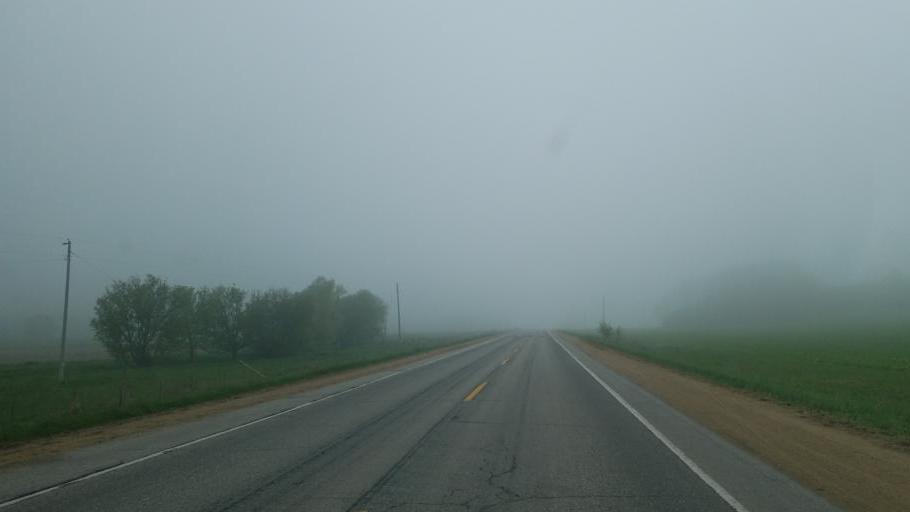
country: US
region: Wisconsin
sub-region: Vernon County
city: Hillsboro
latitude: 43.6265
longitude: -90.3583
